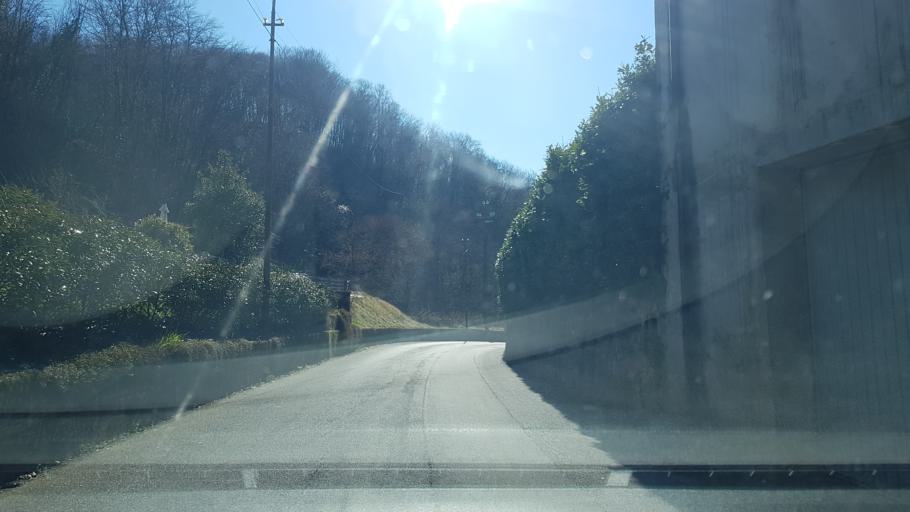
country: IT
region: Friuli Venezia Giulia
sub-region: Provincia di Udine
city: Nimis
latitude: 46.2166
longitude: 13.2938
